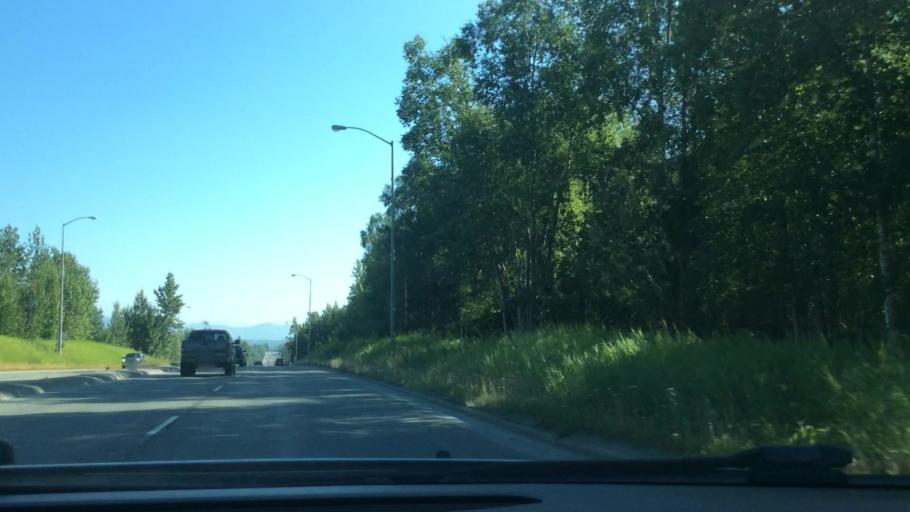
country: US
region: Alaska
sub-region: Anchorage Municipality
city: Anchorage
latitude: 61.2049
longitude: -149.7786
